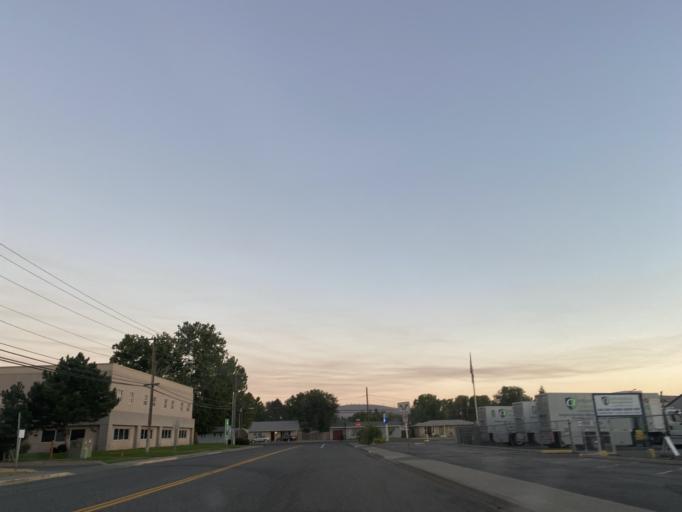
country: US
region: Washington
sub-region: Benton County
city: Kennewick
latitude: 46.1993
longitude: -119.1231
